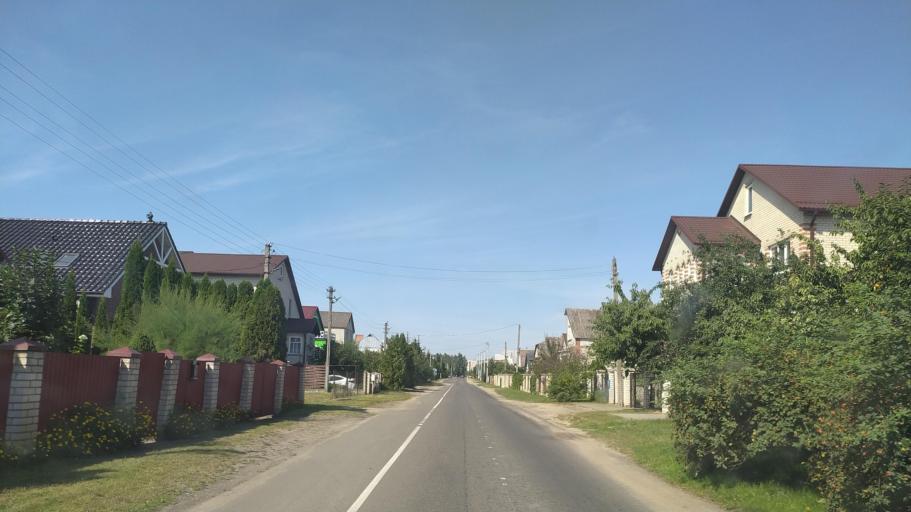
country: BY
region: Brest
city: Byaroza
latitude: 52.5299
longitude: 24.9956
